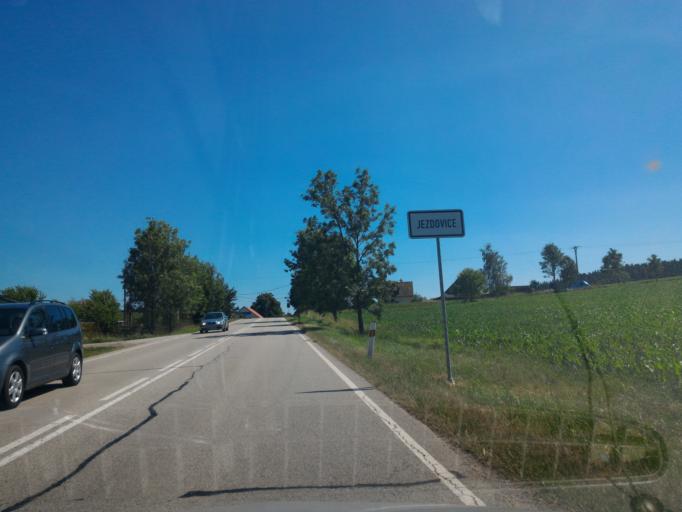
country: CZ
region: Vysocina
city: Dolni Cerekev
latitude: 49.3250
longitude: 15.4818
